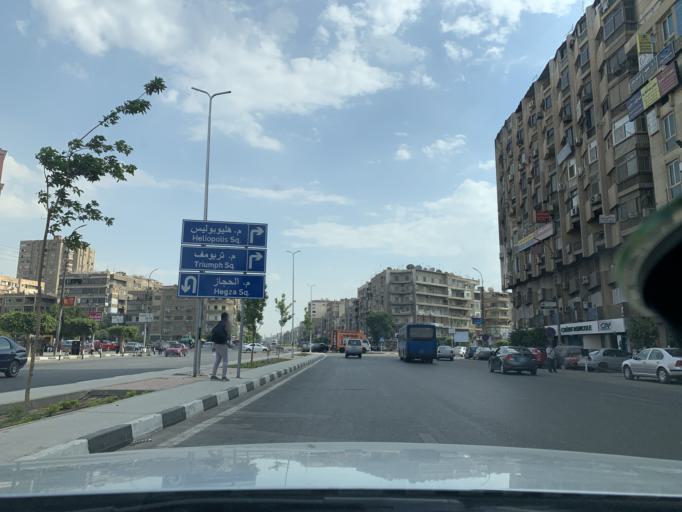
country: EG
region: Muhafazat al Qahirah
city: Cairo
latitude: 30.1064
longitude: 31.3441
